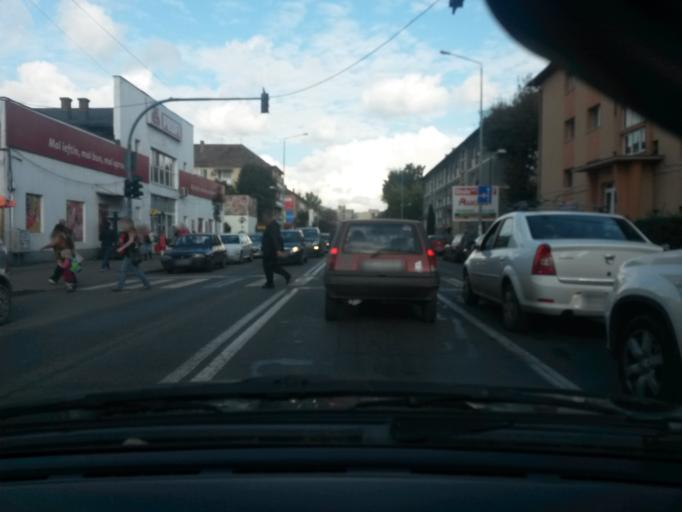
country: RO
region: Mures
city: Targu-Mures
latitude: 46.5559
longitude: 24.5720
